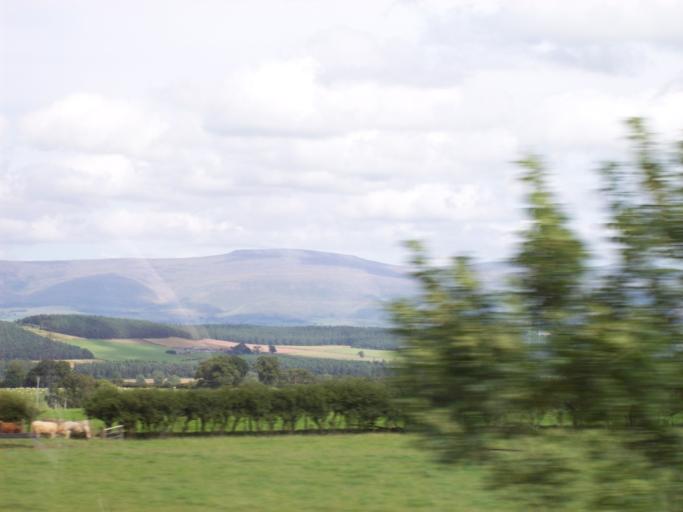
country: GB
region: England
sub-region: Cumbria
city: Penrith
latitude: 54.6110
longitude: -2.7139
